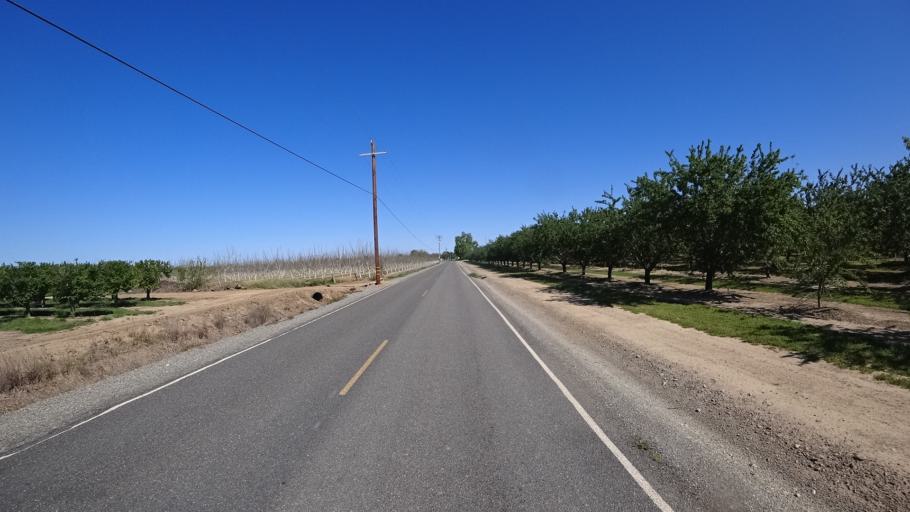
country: US
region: California
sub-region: Glenn County
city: Hamilton City
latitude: 39.7065
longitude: -122.1040
